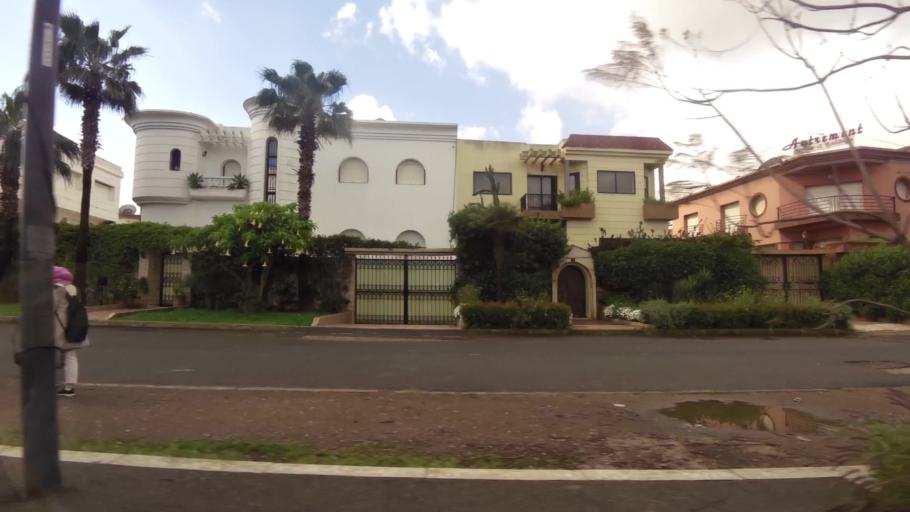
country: MA
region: Grand Casablanca
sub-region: Casablanca
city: Casablanca
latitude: 33.5411
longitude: -7.6478
